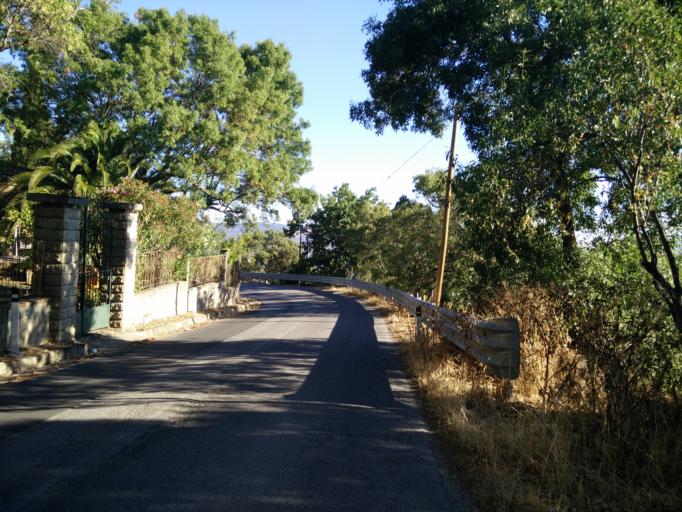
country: IT
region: Sicily
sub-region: Palermo
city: Castelbuono
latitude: 37.9206
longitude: 14.0921
